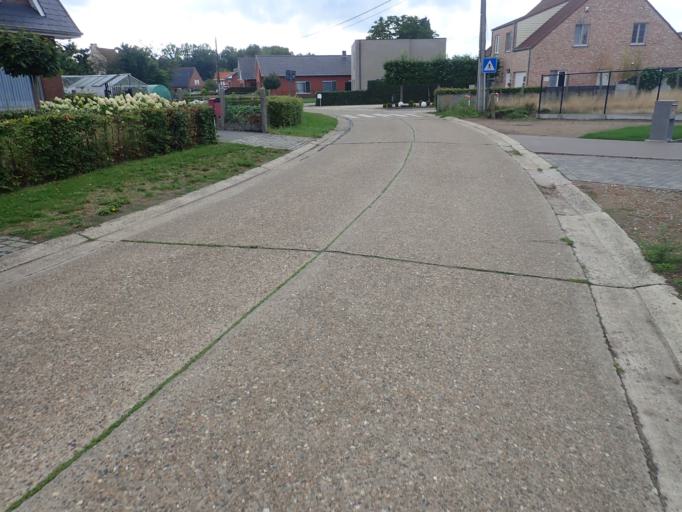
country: BE
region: Flanders
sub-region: Provincie Antwerpen
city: Lille
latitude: 51.2640
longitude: 4.7833
